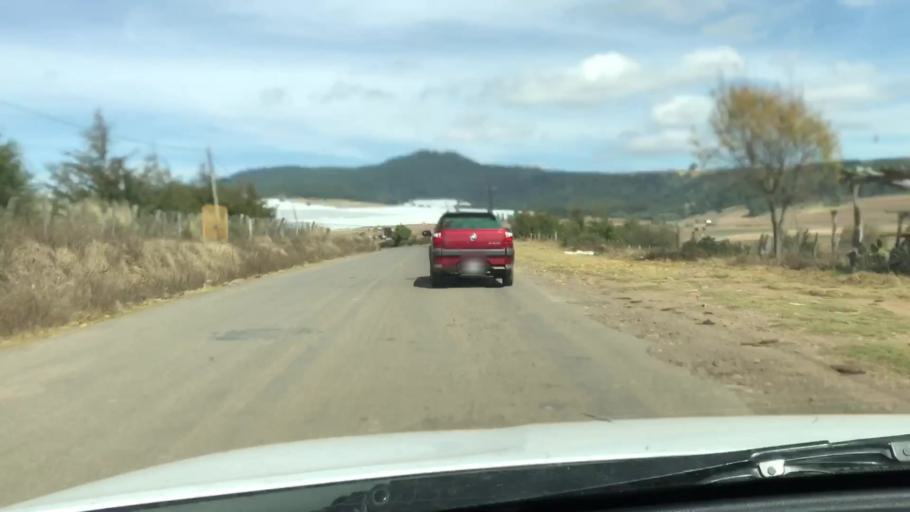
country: MX
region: Jalisco
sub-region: Amacueca
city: Tepec
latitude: 20.0201
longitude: -103.6893
